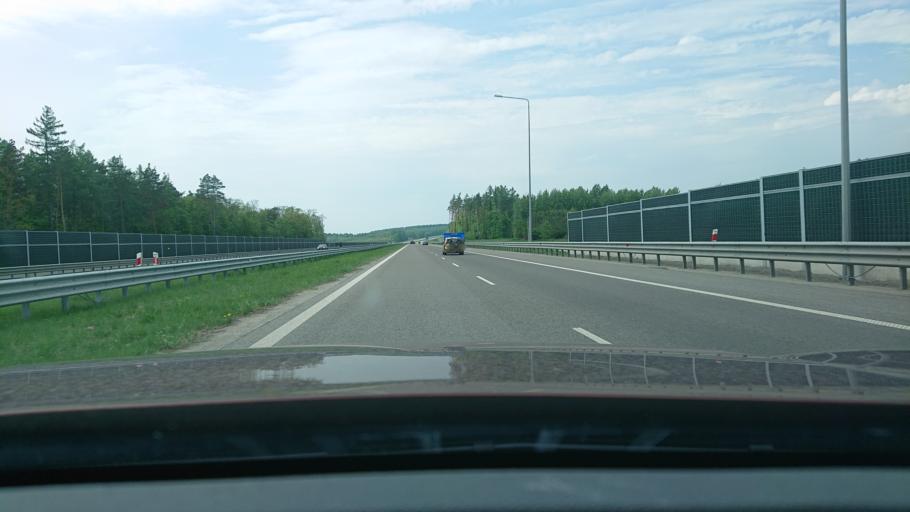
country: PL
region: Subcarpathian Voivodeship
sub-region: Powiat jaroslawski
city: Pawlosiow
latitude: 49.9777
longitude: 22.6316
